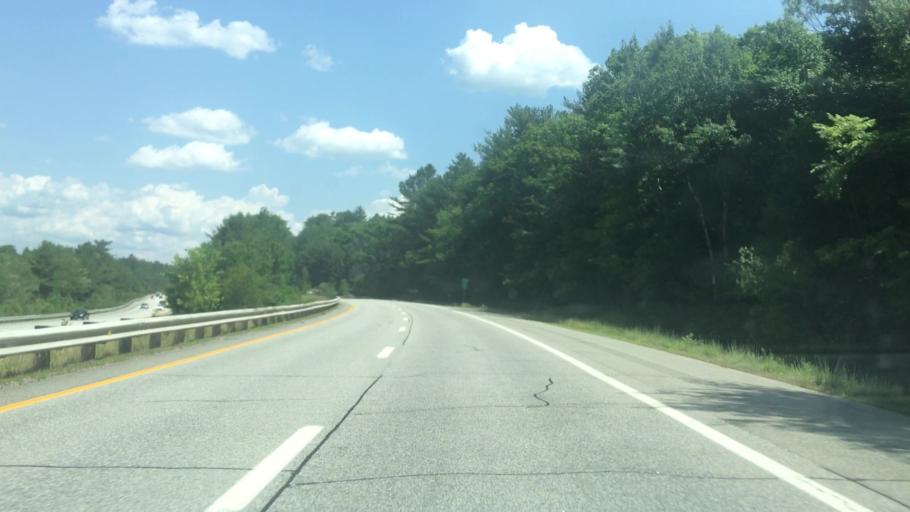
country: US
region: New Hampshire
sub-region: Merrimack County
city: Henniker
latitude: 43.2786
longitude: -71.8252
